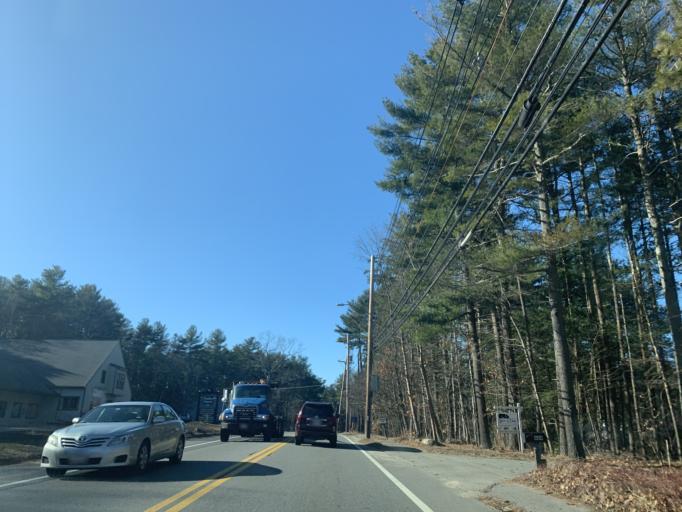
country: US
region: Massachusetts
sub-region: Middlesex County
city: Sudbury
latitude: 42.3603
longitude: -71.4375
